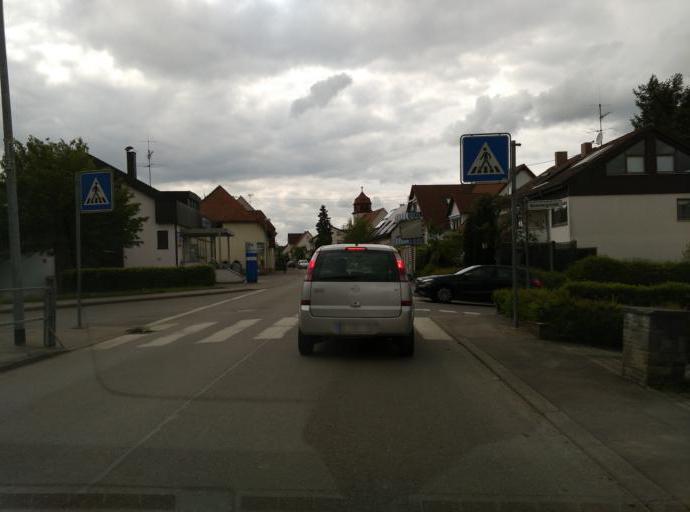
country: DE
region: Baden-Wuerttemberg
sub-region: Regierungsbezirk Stuttgart
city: Grossbettlingen
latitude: 48.6038
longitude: 9.3065
